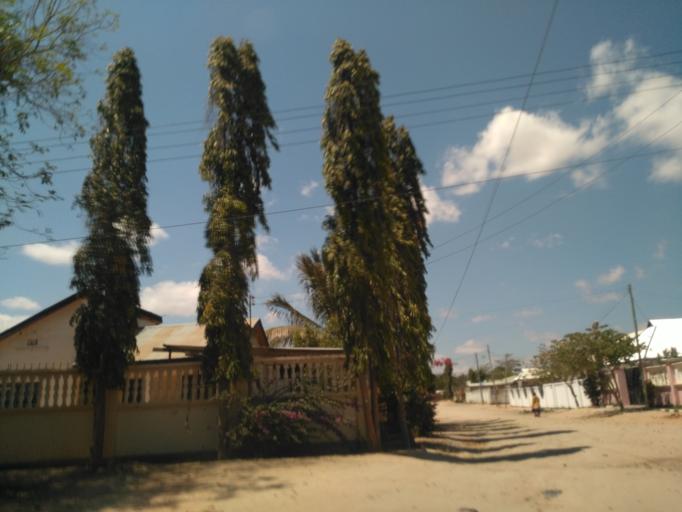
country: TZ
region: Dodoma
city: Kisasa
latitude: -6.1690
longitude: 35.7705
